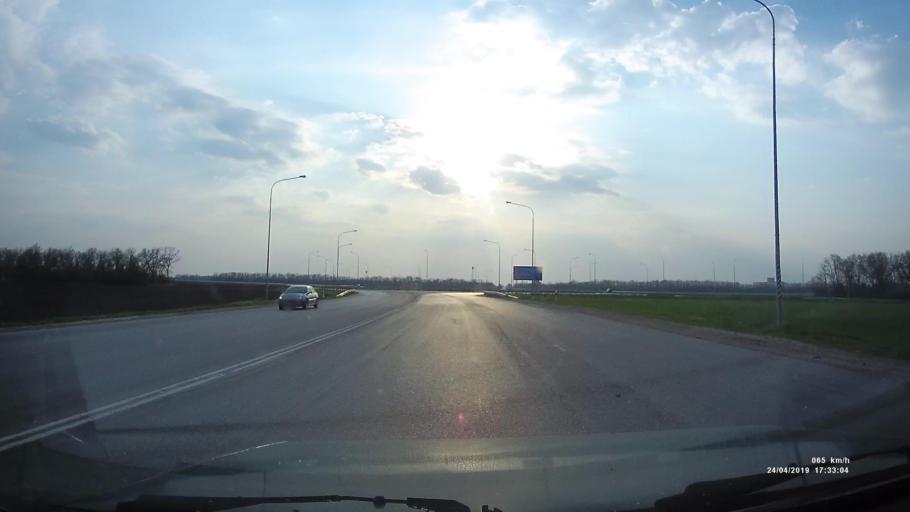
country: RU
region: Rostov
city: Tselina
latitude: 46.5264
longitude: 41.0846
